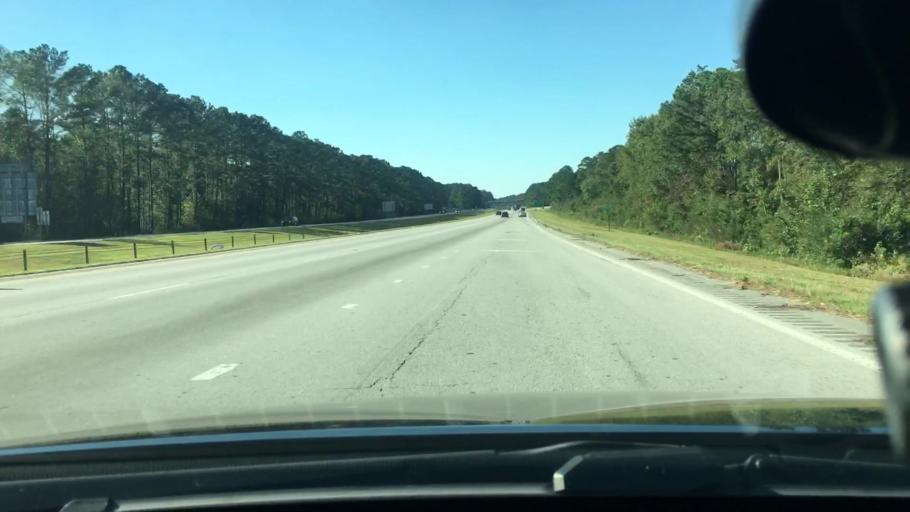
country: US
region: North Carolina
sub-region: Craven County
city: Trent Woods
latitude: 35.1066
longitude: -77.0880
